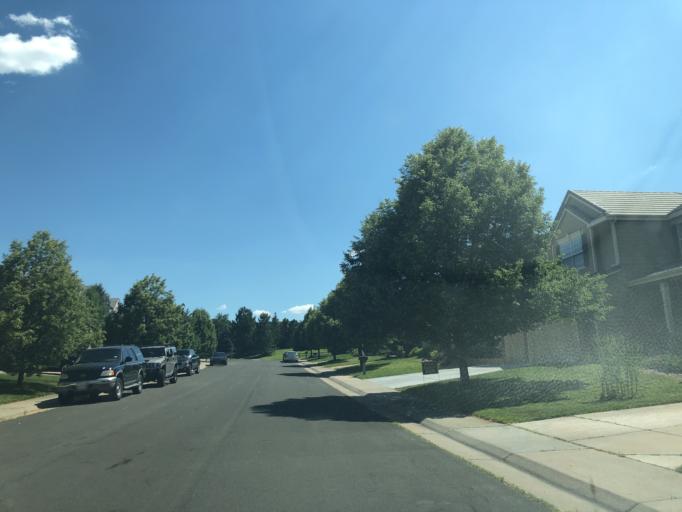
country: US
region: Colorado
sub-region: Arapahoe County
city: Dove Valley
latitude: 39.6046
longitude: -104.7785
